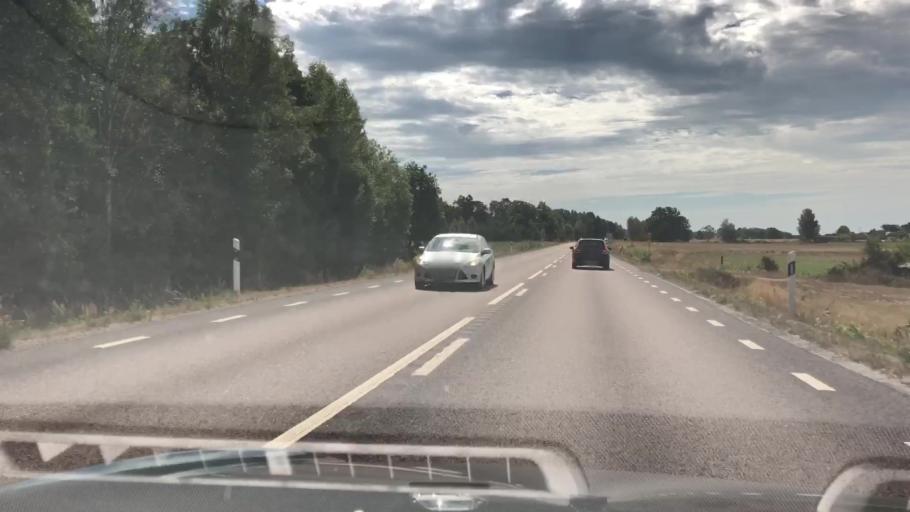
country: SE
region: Kalmar
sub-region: Torsas Kommun
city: Torsas
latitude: 56.3414
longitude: 16.0479
